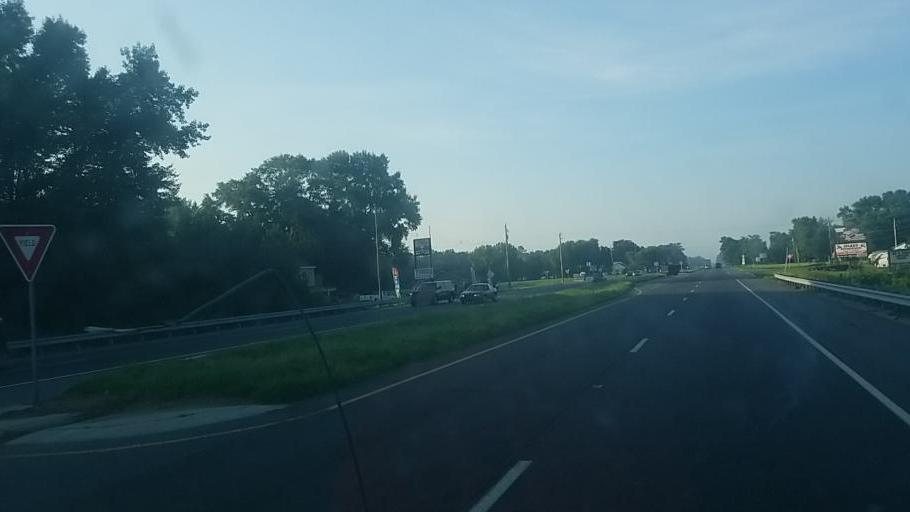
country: US
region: Delaware
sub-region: Sussex County
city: Selbyville
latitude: 38.5026
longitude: -75.2375
